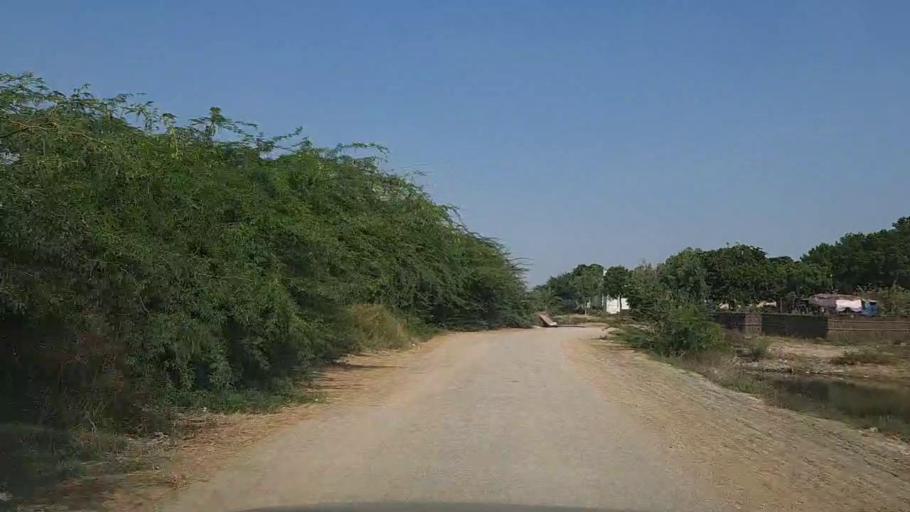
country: PK
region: Sindh
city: Thatta
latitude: 24.6182
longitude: 67.9597
